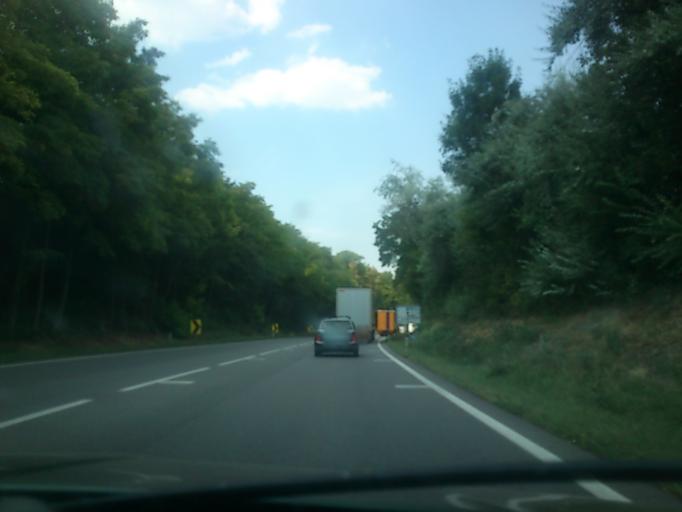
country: AT
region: Lower Austria
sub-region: Politischer Bezirk Mistelbach
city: Drasenhofen
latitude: 48.7463
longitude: 16.6509
